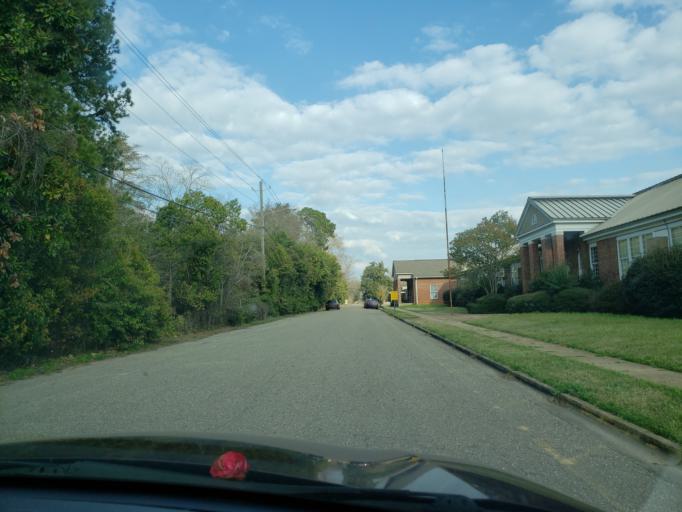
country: US
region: Alabama
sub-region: Hale County
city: Greensboro
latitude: 32.7029
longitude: -87.6007
